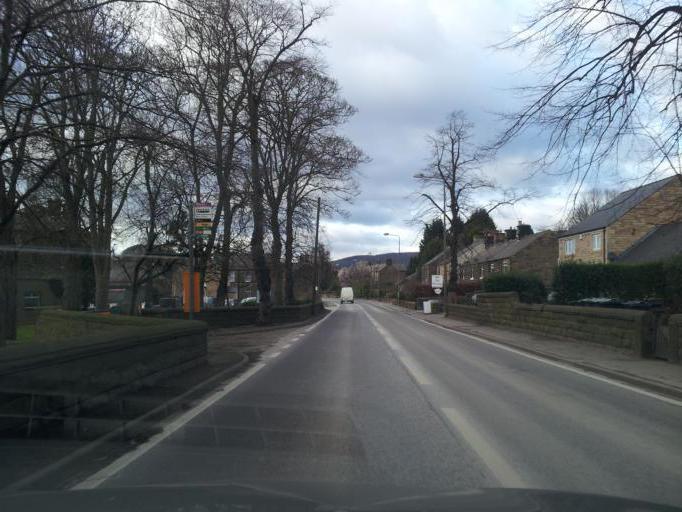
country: GB
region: England
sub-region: Derbyshire
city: Matlock
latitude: 53.1749
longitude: -1.6073
